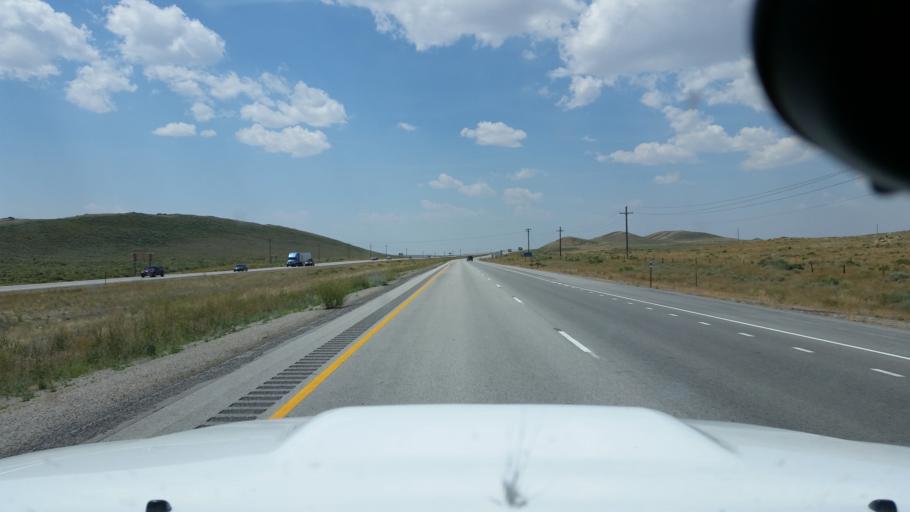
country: US
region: Wyoming
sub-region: Carbon County
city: Rawlins
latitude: 41.7765
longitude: -107.3171
